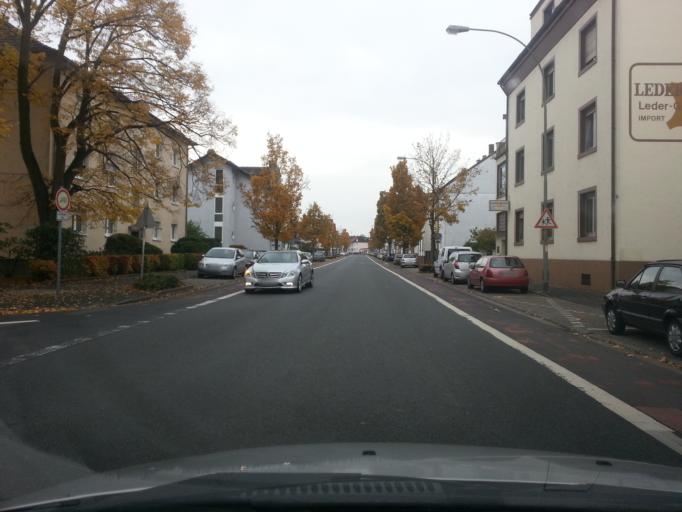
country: DE
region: Hesse
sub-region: Regierungsbezirk Darmstadt
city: Muehlheim am Main
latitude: 50.1237
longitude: 8.8388
